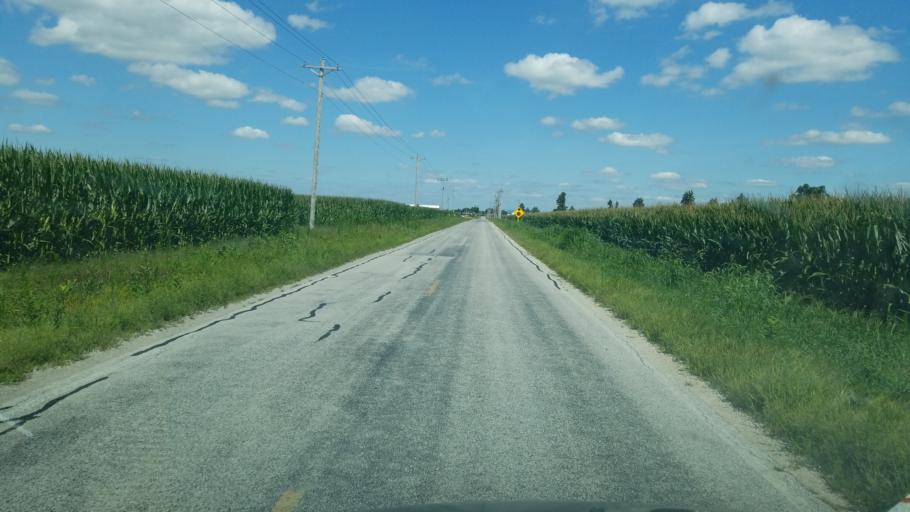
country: US
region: Ohio
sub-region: Fulton County
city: Swanton
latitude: 41.5706
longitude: -83.9408
